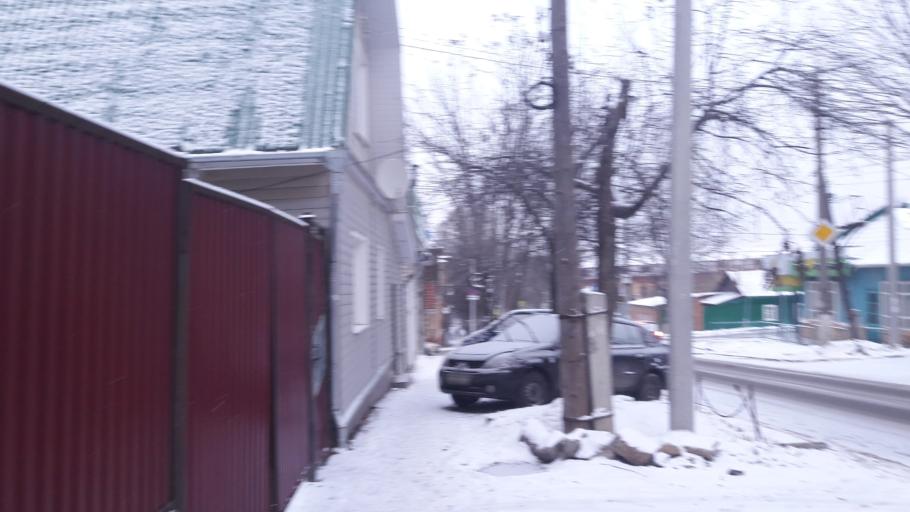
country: RU
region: Tula
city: Tula
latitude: 54.1855
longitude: 37.6149
